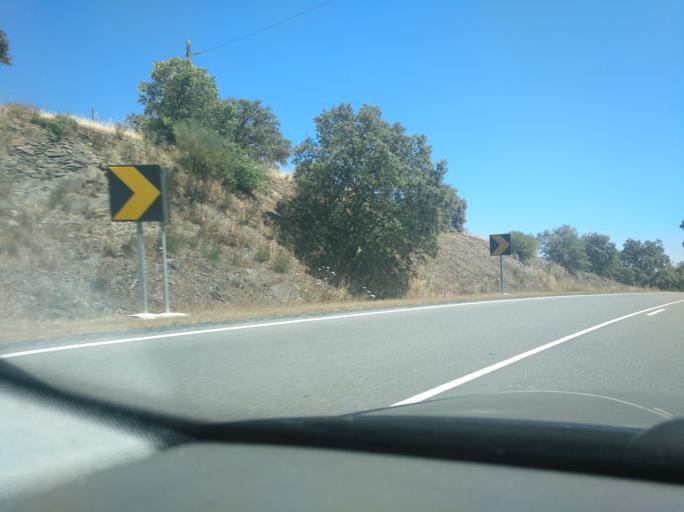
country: PT
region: Beja
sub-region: Castro Verde
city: Castro Verde
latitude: 37.6681
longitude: -8.0809
